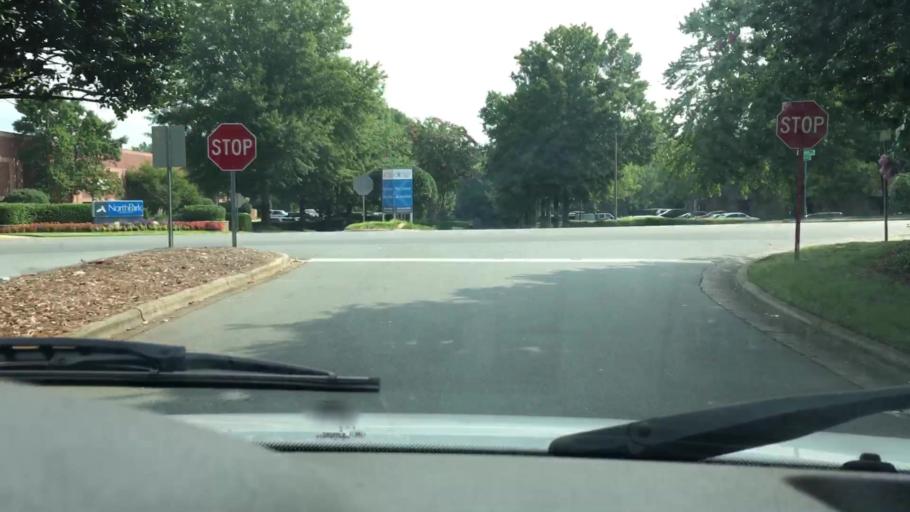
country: US
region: North Carolina
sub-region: Mecklenburg County
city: Charlotte
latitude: 35.3132
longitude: -80.8508
